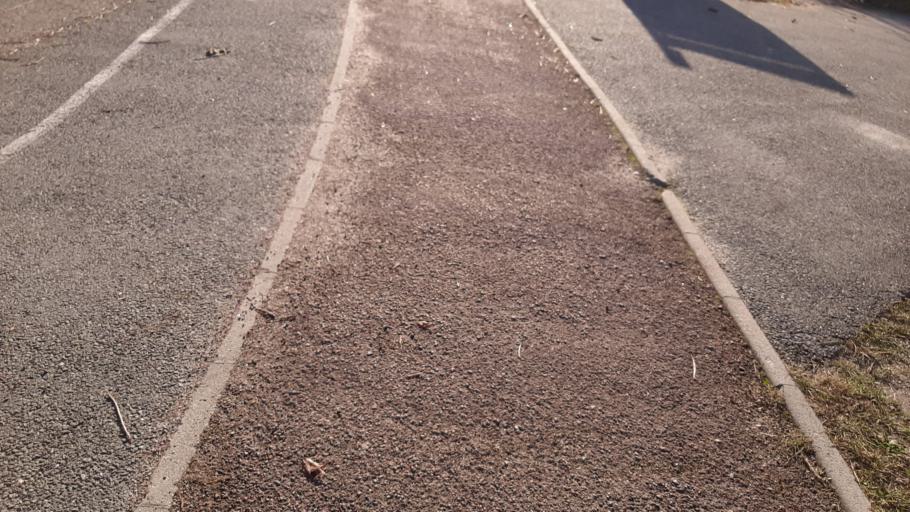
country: FR
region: Aquitaine
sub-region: Departement de la Gironde
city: Merignac
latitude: 44.8307
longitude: -0.6583
